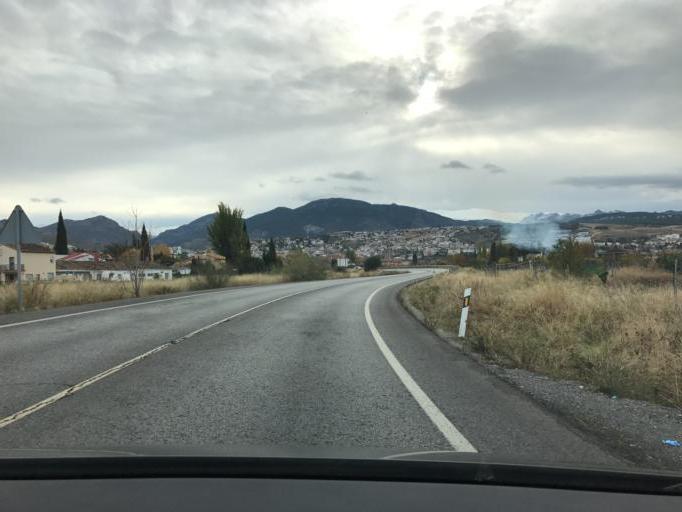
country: ES
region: Andalusia
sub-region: Provincia de Granada
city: Huetor Vega
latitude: 37.1418
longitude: -3.5749
